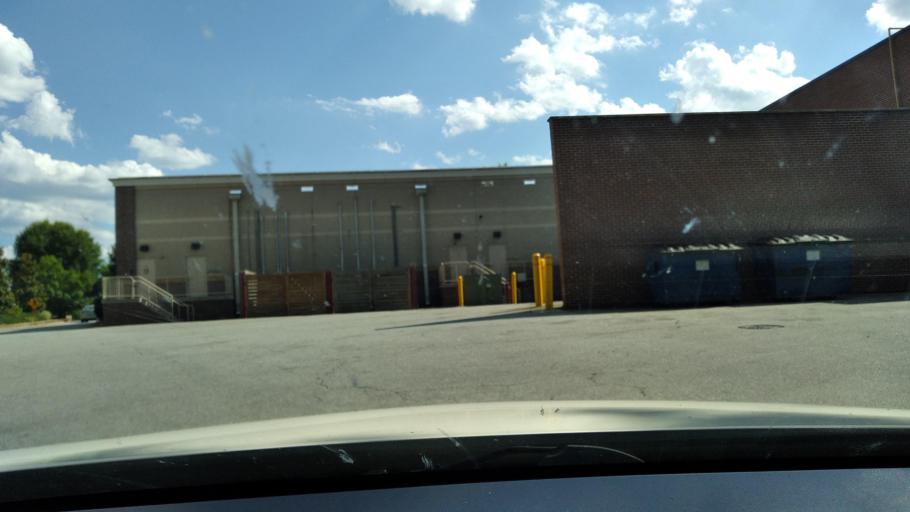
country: US
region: North Carolina
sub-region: Guilford County
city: Greensboro
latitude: 36.0881
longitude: -79.8367
